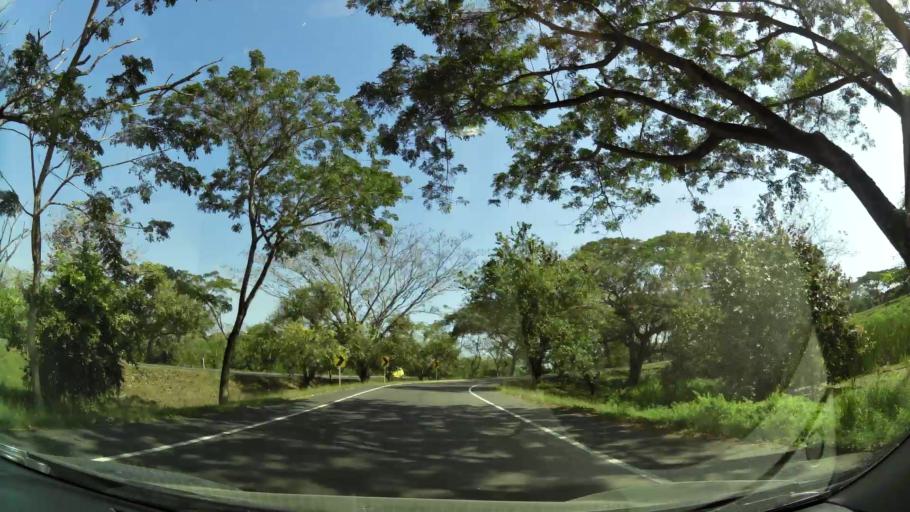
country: CO
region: Bolivar
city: Turbaco
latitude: 10.3716
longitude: -75.4543
